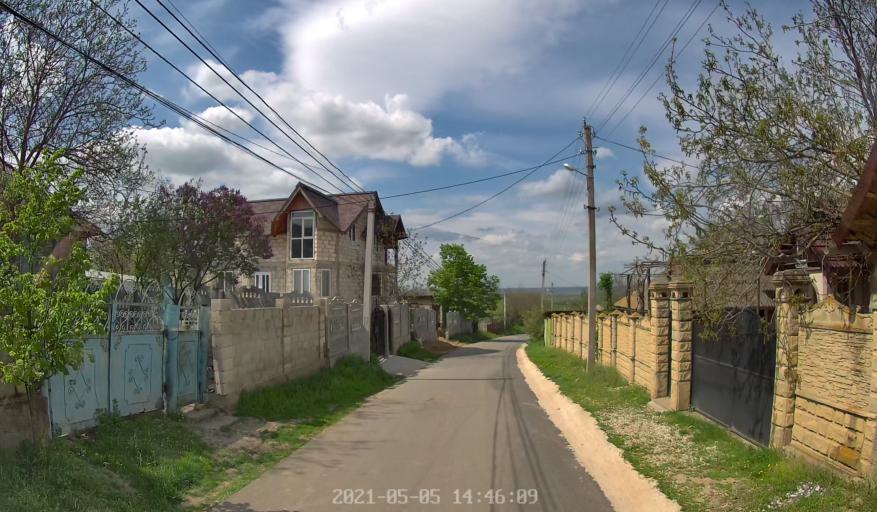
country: MD
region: Chisinau
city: Vadul lui Voda
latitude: 47.0925
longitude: 29.1737
